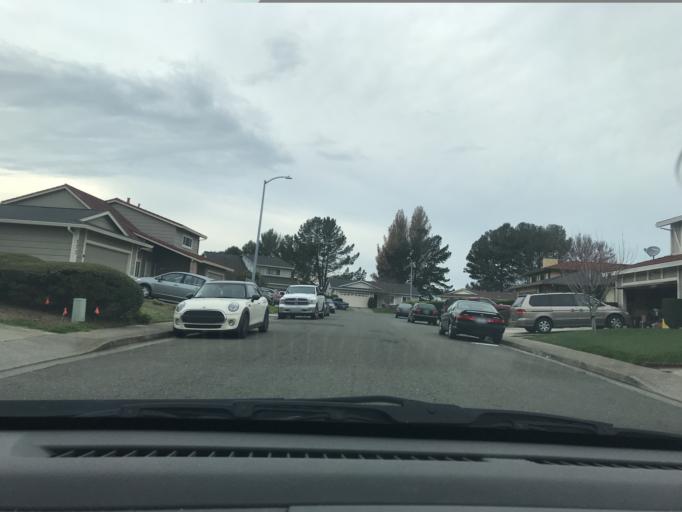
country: US
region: California
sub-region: Solano County
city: Vallejo
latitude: 38.1236
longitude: -122.2190
